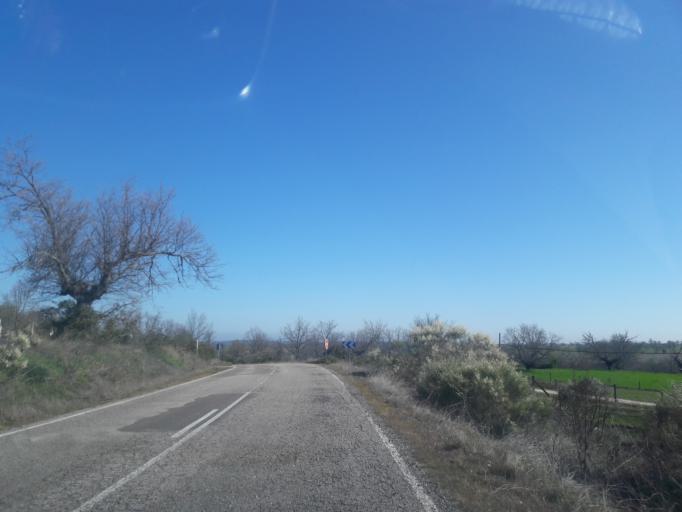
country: ES
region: Castille and Leon
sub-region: Provincia de Salamanca
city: Cabeza del Caballo
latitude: 41.1432
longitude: -6.5574
